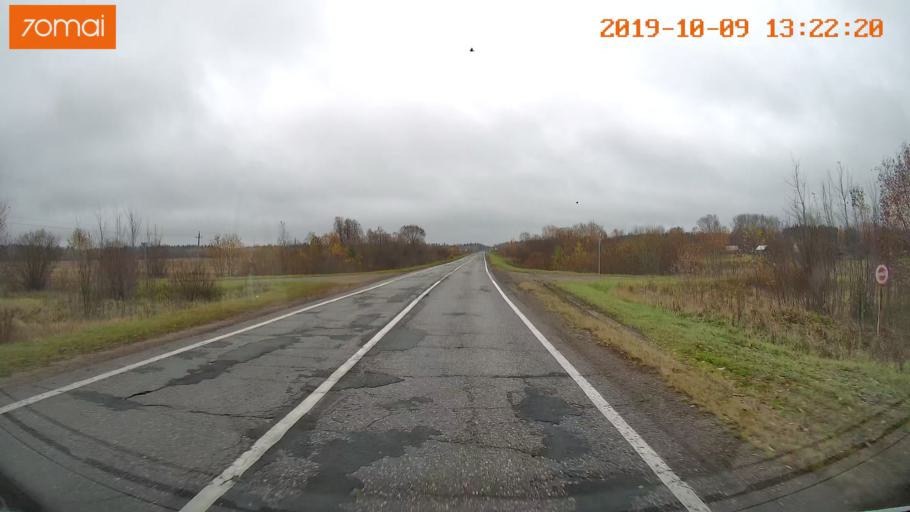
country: RU
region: Jaroslavl
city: Lyubim
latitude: 58.3405
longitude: 40.8628
